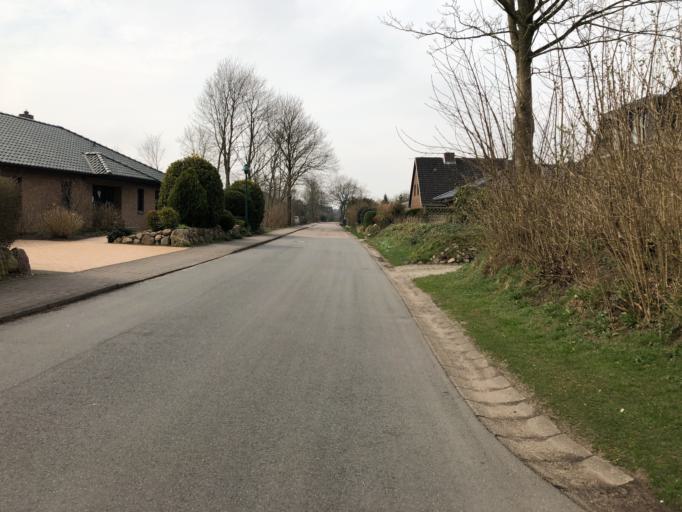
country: DE
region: Schleswig-Holstein
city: Wanderup
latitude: 54.6868
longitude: 9.3298
